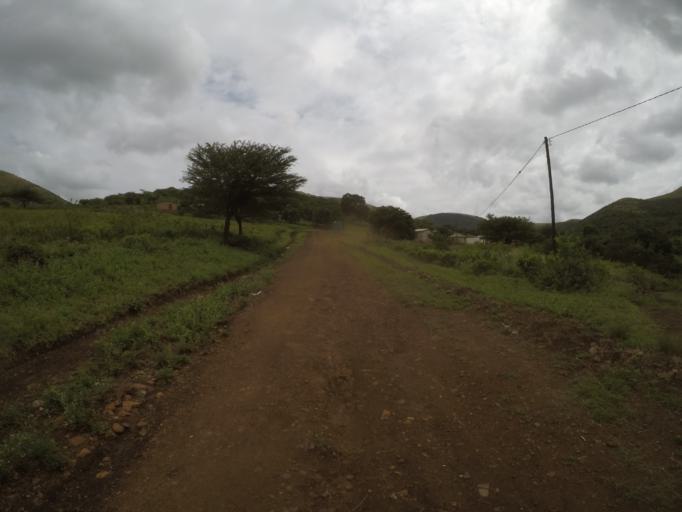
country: ZA
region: KwaZulu-Natal
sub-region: uThungulu District Municipality
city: Empangeni
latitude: -28.5826
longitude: 31.8892
